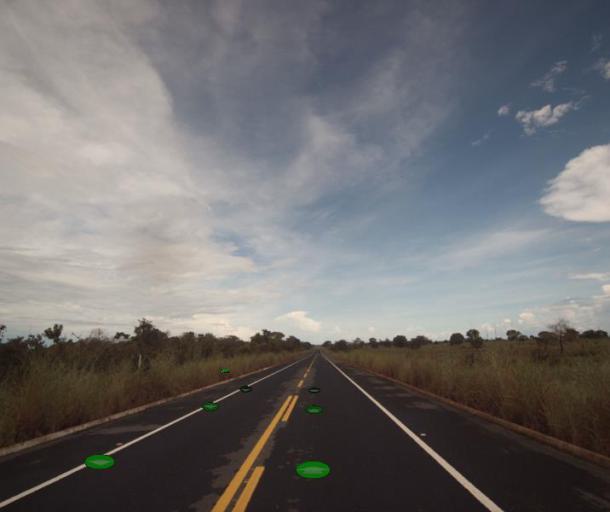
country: BR
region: Goias
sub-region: Sao Miguel Do Araguaia
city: Sao Miguel do Araguaia
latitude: -13.2724
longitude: -50.5046
